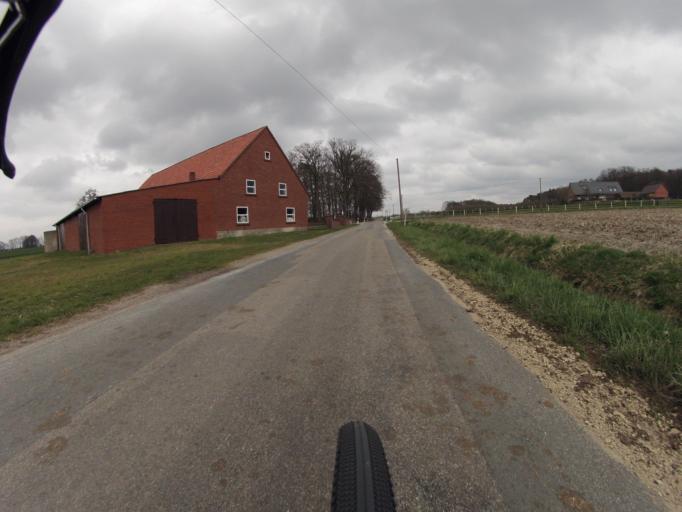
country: DE
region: North Rhine-Westphalia
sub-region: Regierungsbezirk Munster
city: Mettingen
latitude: 52.3297
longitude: 7.8220
